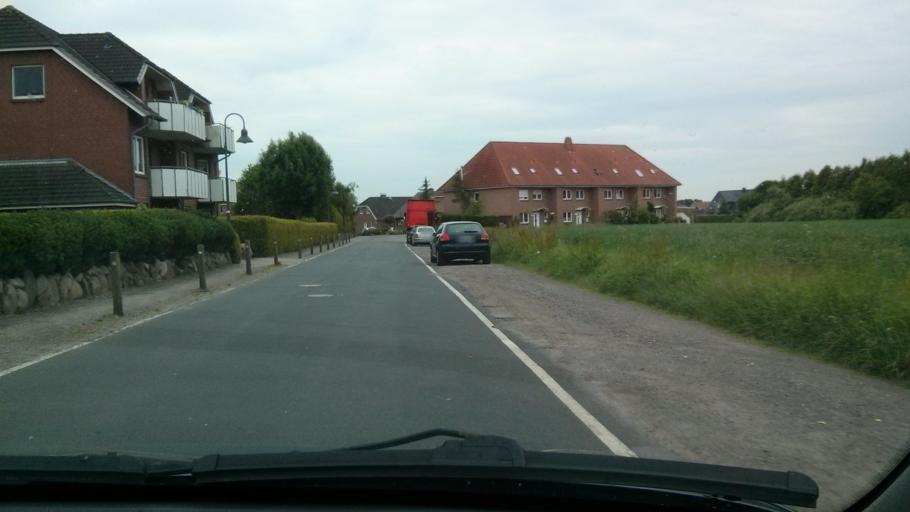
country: DE
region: Lower Saxony
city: Loxstedt
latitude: 53.4669
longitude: 8.6468
